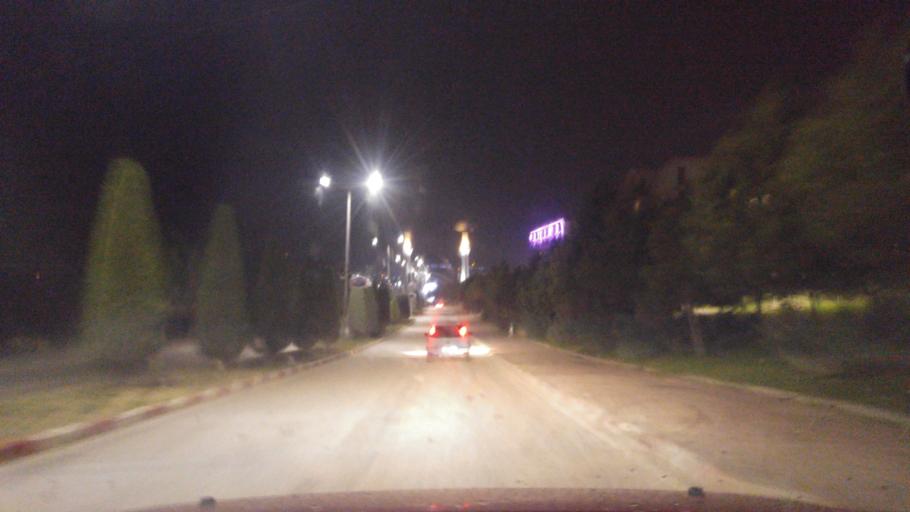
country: TR
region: Karabuk
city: Karabuk
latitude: 41.2091
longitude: 32.6565
